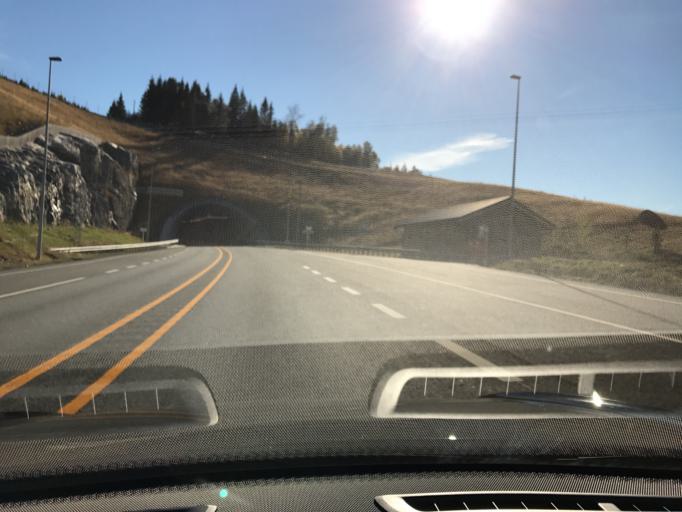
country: NO
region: Buskerud
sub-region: Krodsherad
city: Noresund
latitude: 60.2928
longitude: 9.6825
